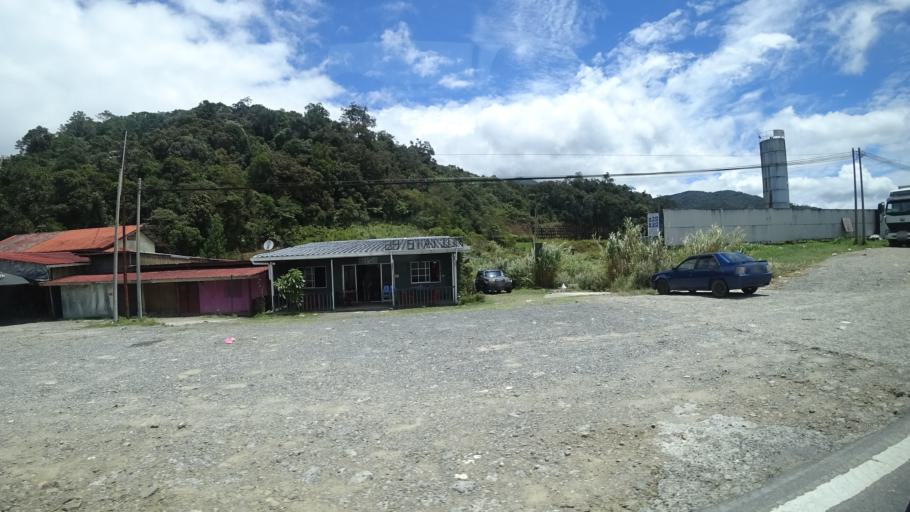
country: MY
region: Sabah
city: Ranau
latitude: 6.0042
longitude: 116.5464
